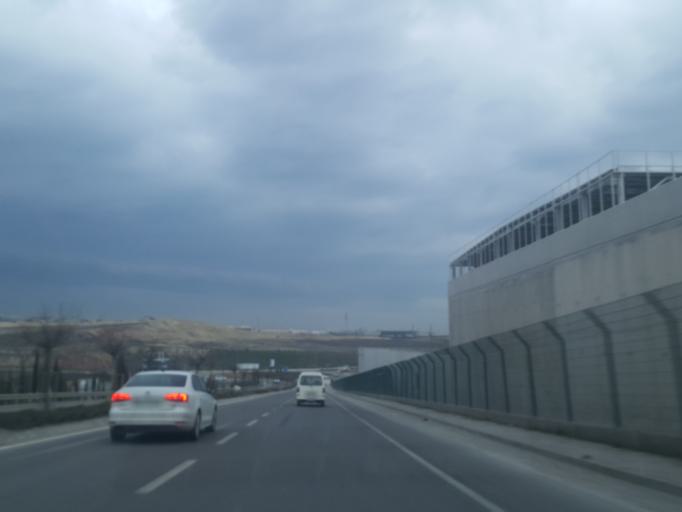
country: TR
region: Kocaeli
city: Tavsanli
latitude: 40.8247
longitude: 29.5592
